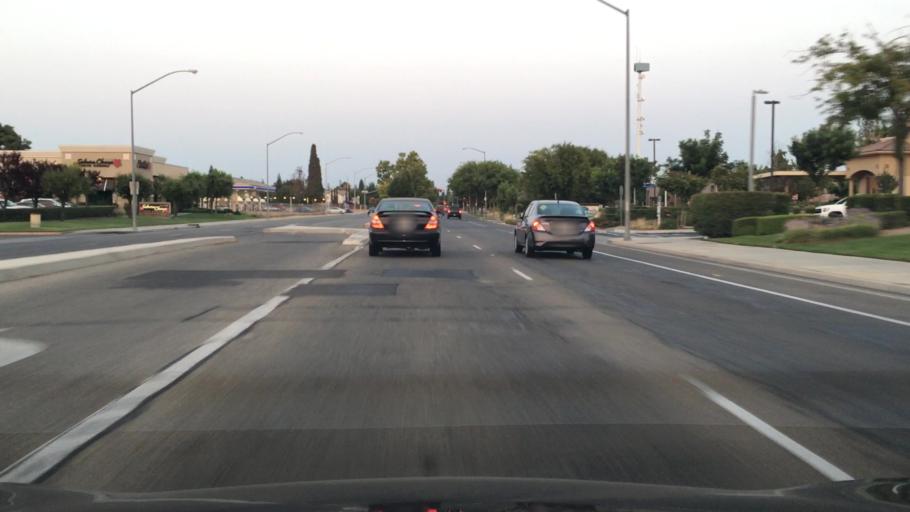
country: US
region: California
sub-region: Fresno County
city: Clovis
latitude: 36.8519
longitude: -119.7731
